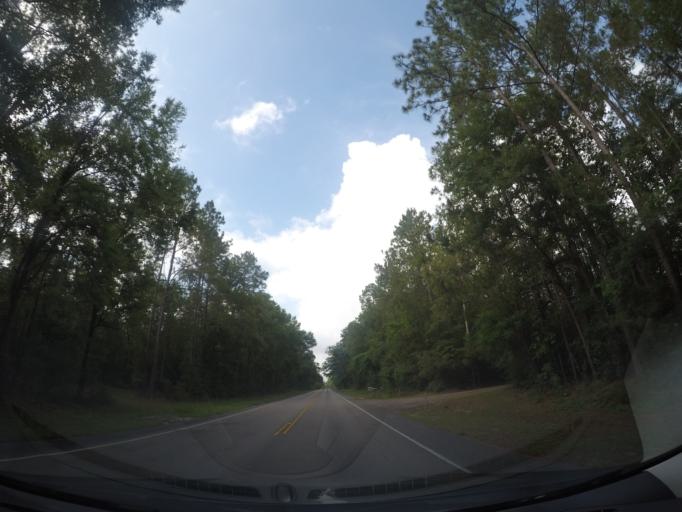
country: US
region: Florida
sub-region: Leon County
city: Woodville
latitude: 30.2678
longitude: -84.3128
